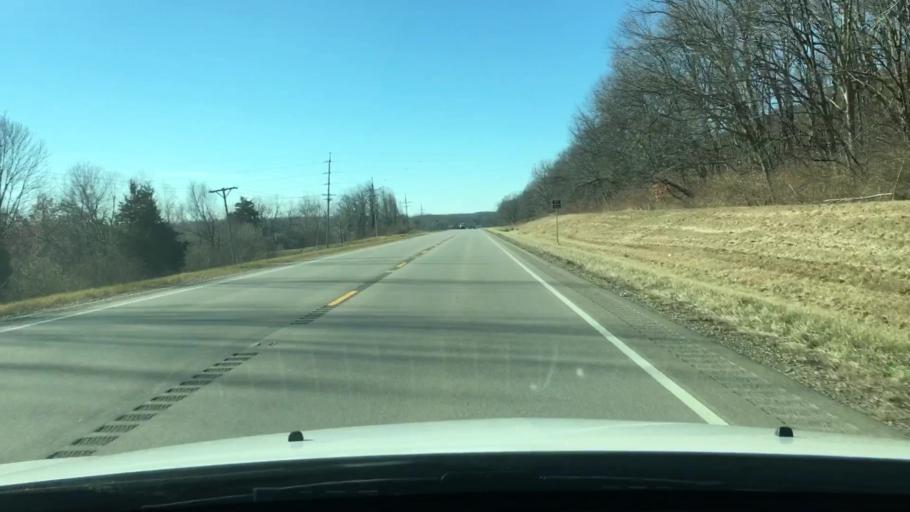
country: US
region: Illinois
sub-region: Peoria County
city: Glasford
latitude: 40.5221
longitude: -89.8855
